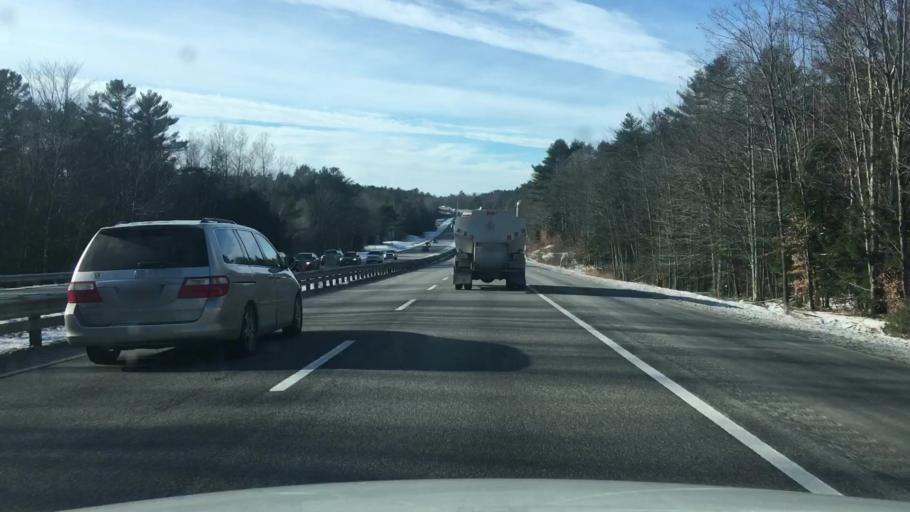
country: US
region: Maine
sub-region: Cumberland County
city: Freeport
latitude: 43.9048
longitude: -70.0616
